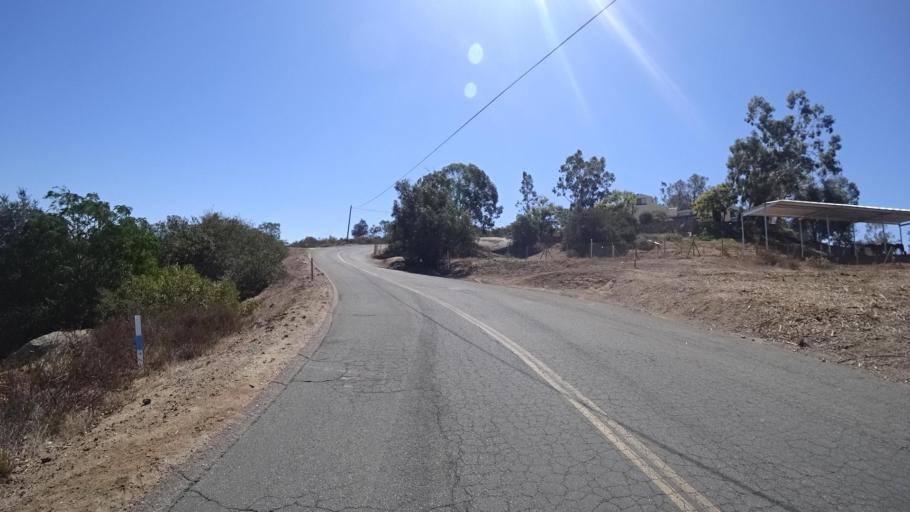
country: US
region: California
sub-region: San Diego County
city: Valley Center
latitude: 33.2832
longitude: -116.9932
